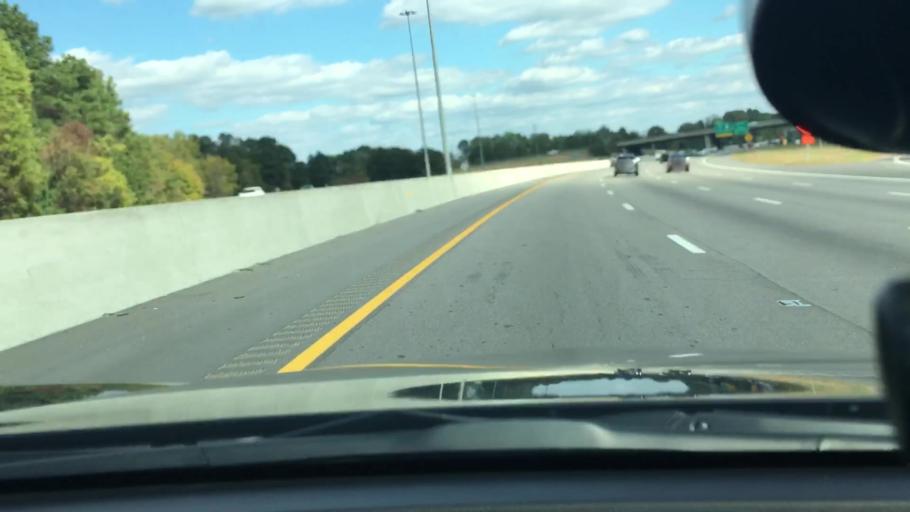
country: US
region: North Carolina
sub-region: Wake County
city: Raleigh
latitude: 35.7569
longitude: -78.6170
